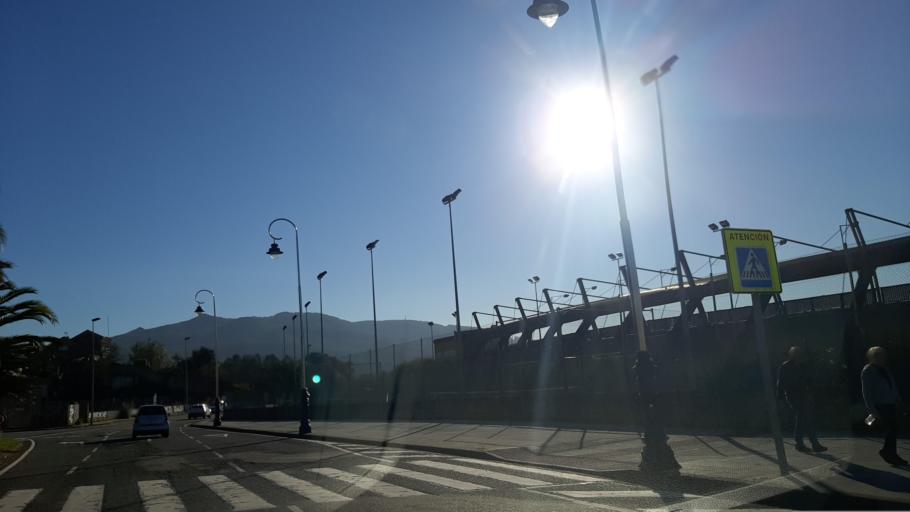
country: ES
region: Galicia
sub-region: Provincia de Pontevedra
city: Cangas
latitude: 42.2038
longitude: -8.7770
